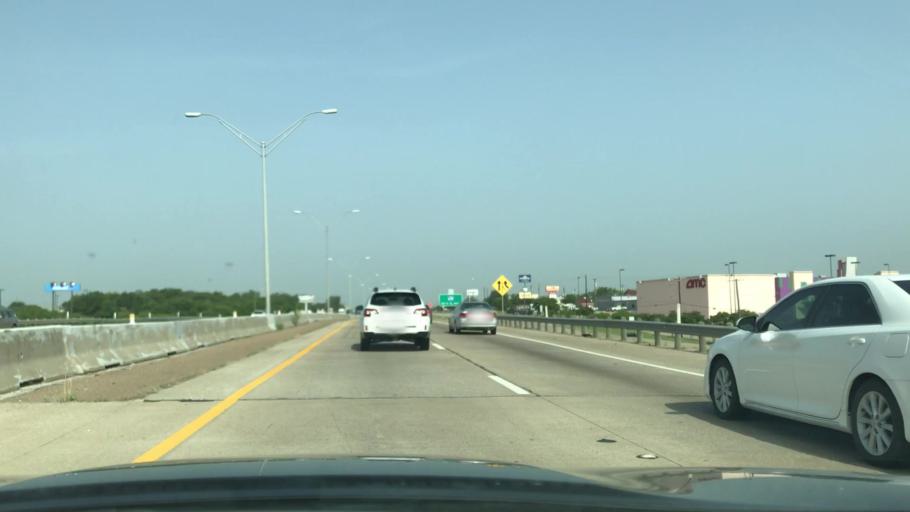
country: US
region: Texas
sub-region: Dallas County
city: Mesquite
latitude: 32.7907
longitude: -96.5962
